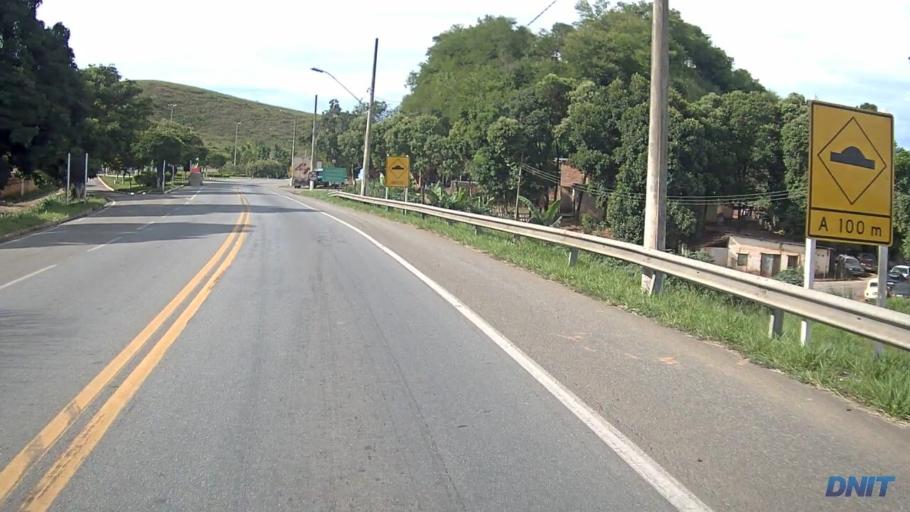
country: BR
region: Minas Gerais
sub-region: Belo Oriente
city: Belo Oriente
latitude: -19.1586
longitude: -42.2378
